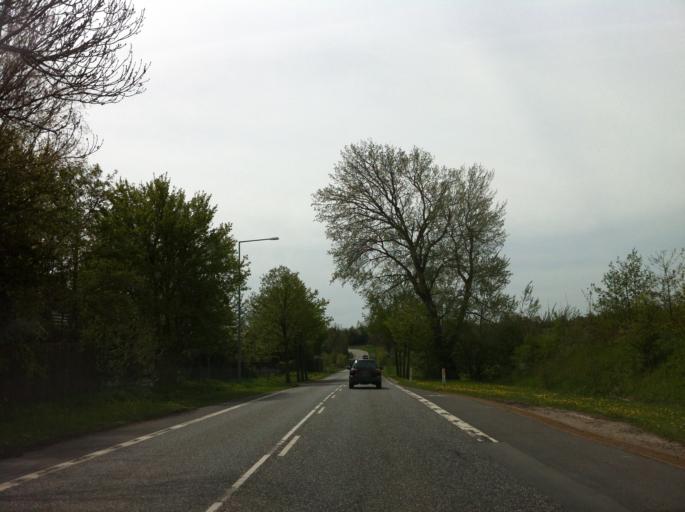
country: DK
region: Zealand
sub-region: Ringsted Kommune
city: Ringsted
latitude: 55.3904
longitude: 11.7650
